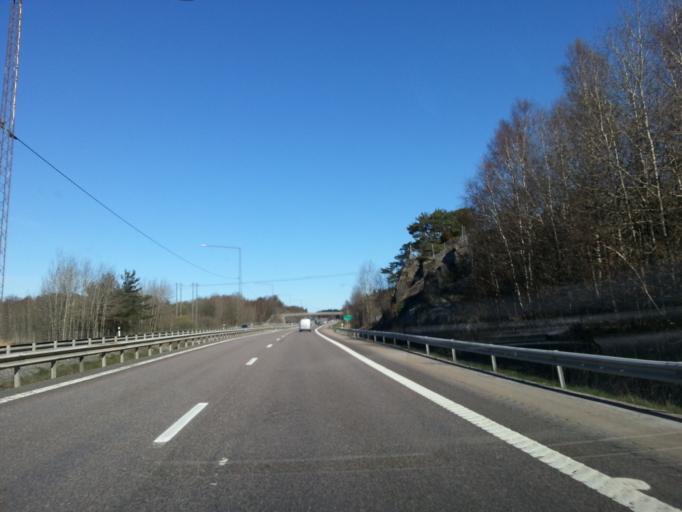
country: SE
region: Vaestra Goetaland
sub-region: Kungalvs Kommun
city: Kode
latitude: 57.9488
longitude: 11.8531
